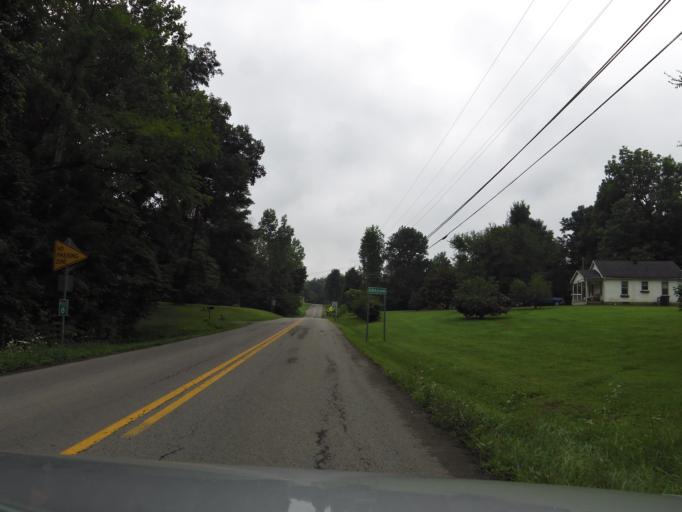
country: US
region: Kentucky
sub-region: Muhlenberg County
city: Morehead
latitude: 37.2588
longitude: -87.2822
